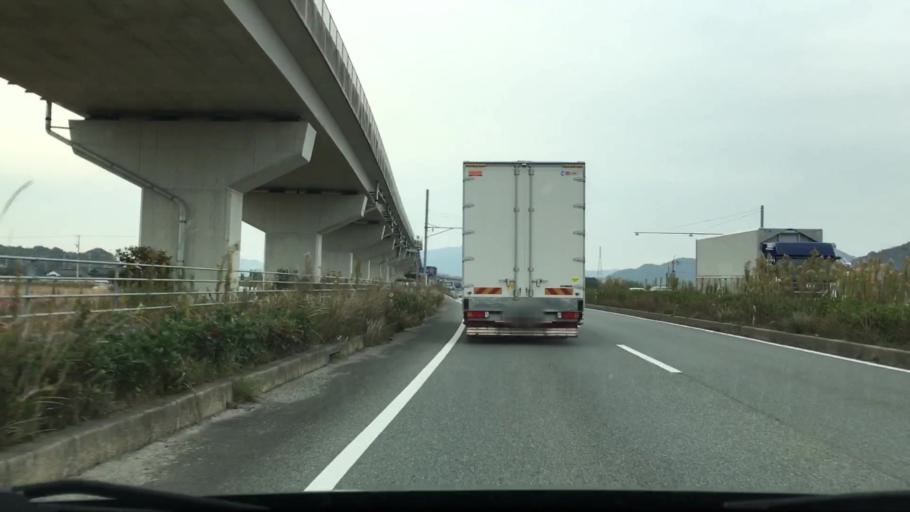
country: JP
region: Yamaguchi
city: Ogori-shimogo
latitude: 34.0815
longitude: 131.4500
